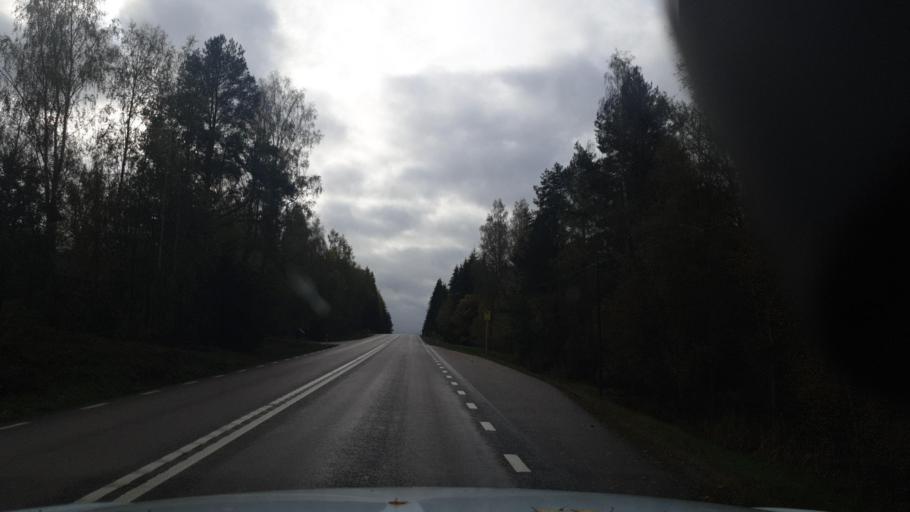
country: SE
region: Vaermland
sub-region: Sunne Kommun
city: Sunne
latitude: 59.6430
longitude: 12.9447
